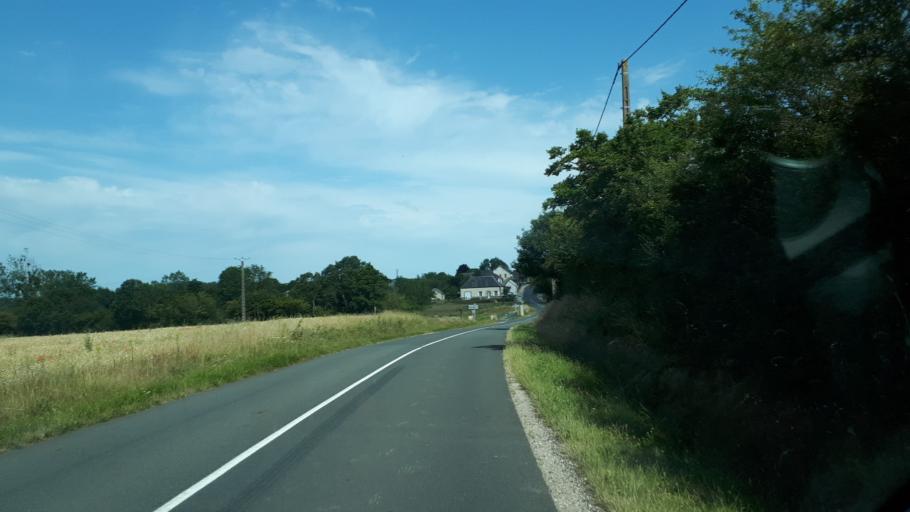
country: FR
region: Centre
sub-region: Departement du Loir-et-Cher
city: Droue
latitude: 47.9873
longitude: 1.0363
